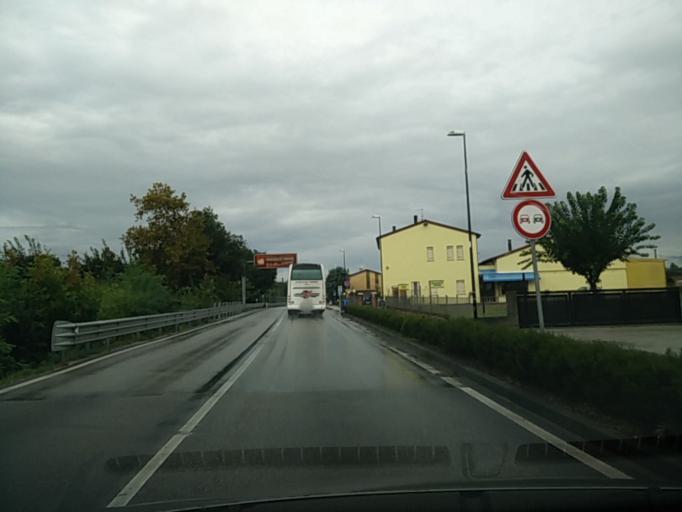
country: IT
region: Veneto
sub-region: Provincia di Vicenza
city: Rossano Veneto
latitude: 45.7011
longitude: 11.8218
